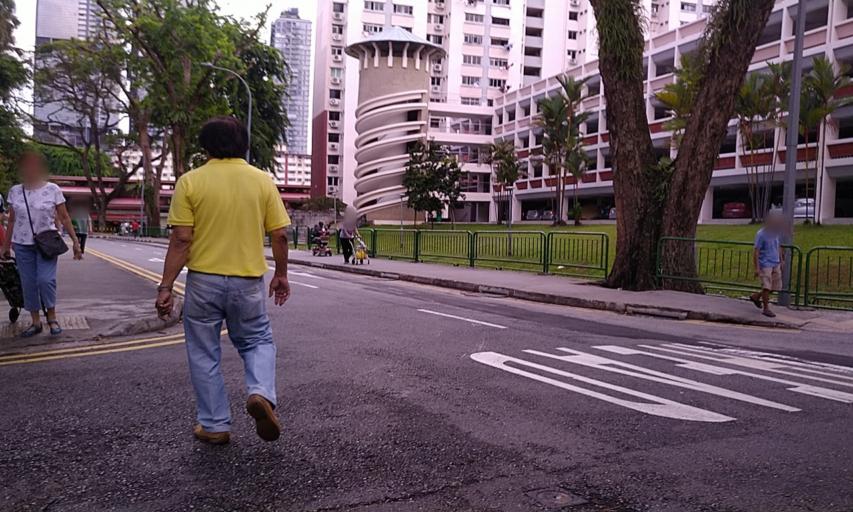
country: SG
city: Singapore
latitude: 1.2861
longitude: 103.8182
